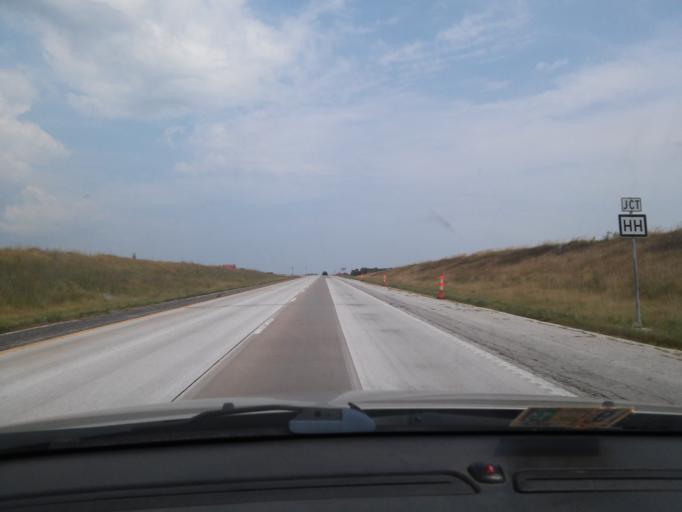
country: US
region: Missouri
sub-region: Audrain County
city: Mexico
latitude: 39.0669
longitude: -91.8958
